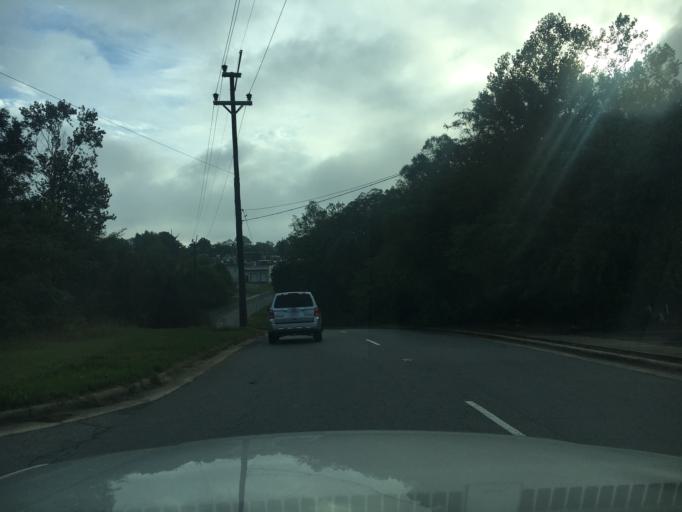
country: US
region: North Carolina
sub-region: Catawba County
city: Hickory
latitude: 35.7295
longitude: -81.3570
